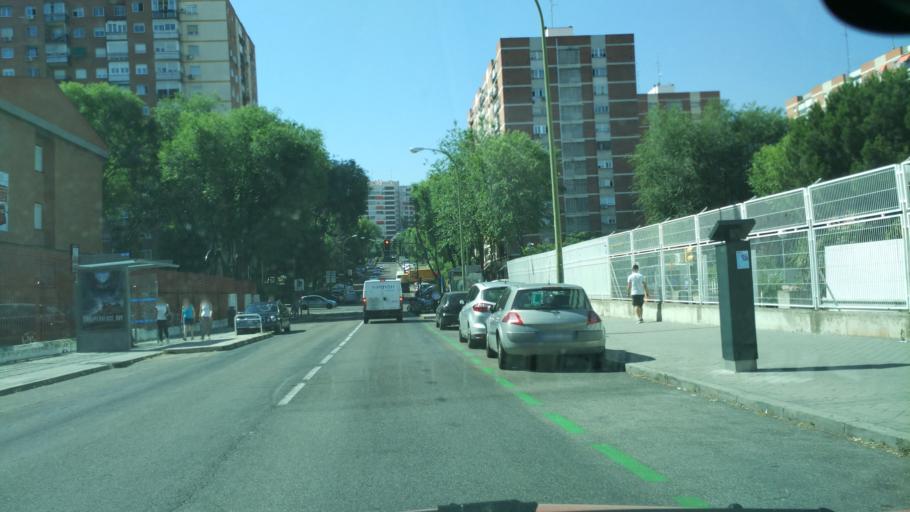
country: ES
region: Madrid
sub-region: Provincia de Madrid
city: Tetuan de las Victorias
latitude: 40.4805
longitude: -3.7030
